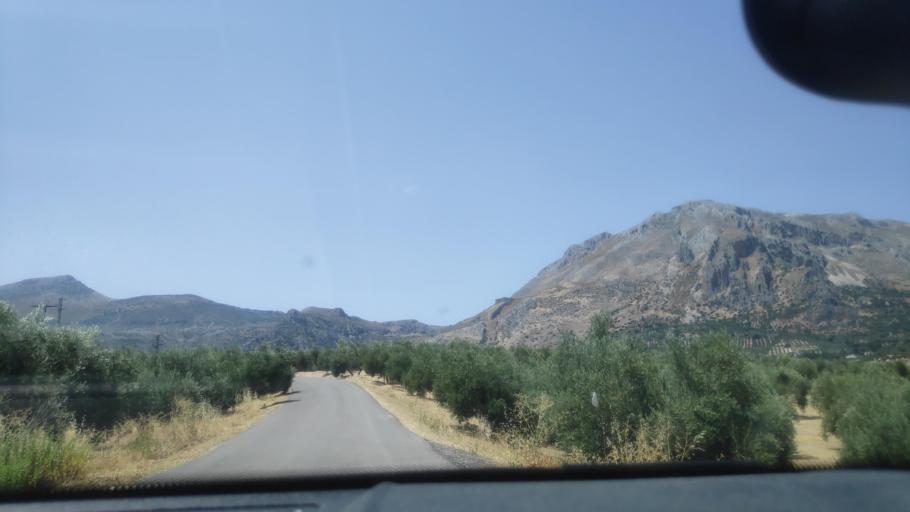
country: ES
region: Andalusia
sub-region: Provincia de Jaen
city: Jimena
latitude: 37.8035
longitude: -3.4416
